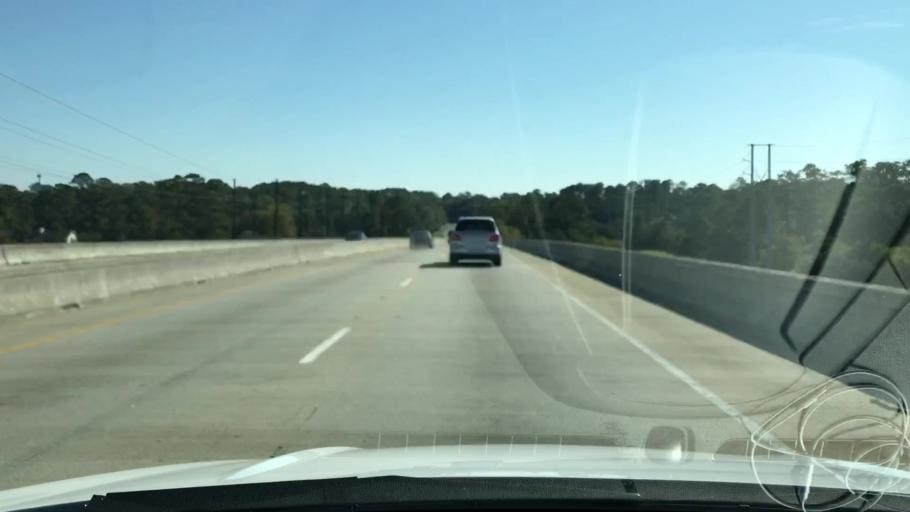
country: US
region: South Carolina
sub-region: Beaufort County
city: Hilton Head Island
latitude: 32.2236
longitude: -80.7809
